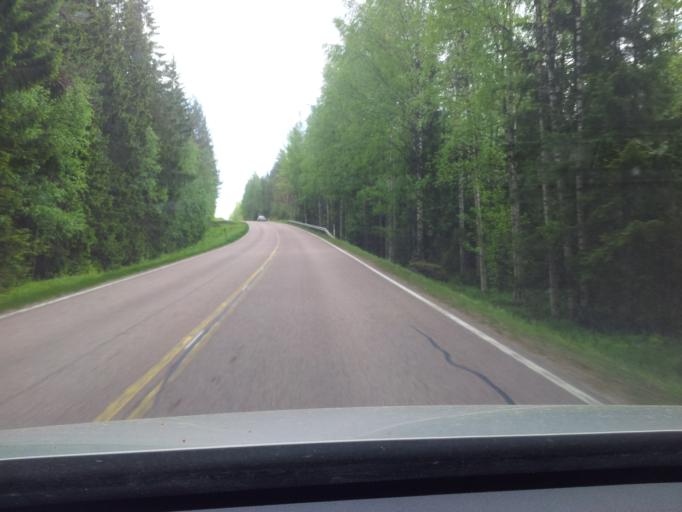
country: FI
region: South Karelia
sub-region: Lappeenranta
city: Luumaeki
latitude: 60.9682
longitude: 27.5620
